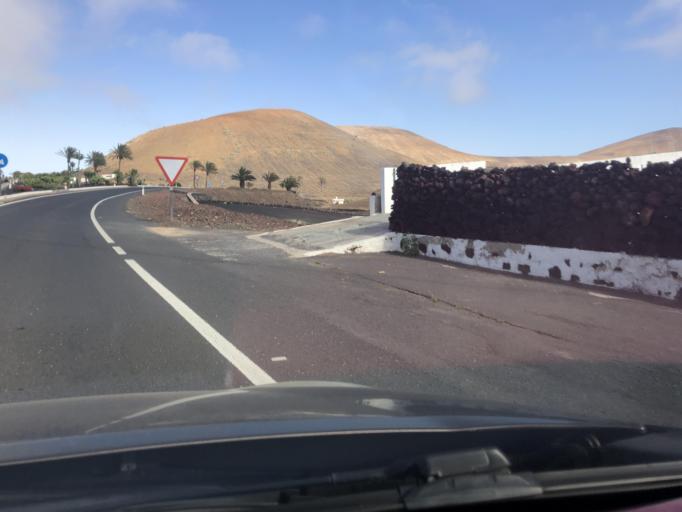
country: ES
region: Canary Islands
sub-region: Provincia de Las Palmas
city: Yaiza
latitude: 28.9516
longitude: -13.7596
